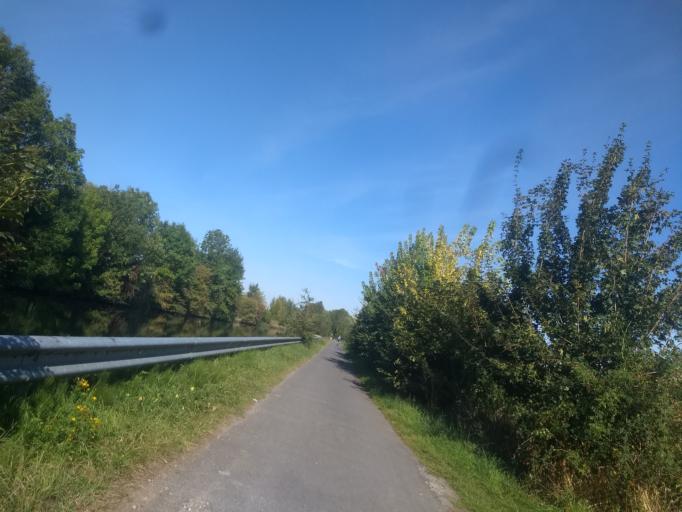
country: FR
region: Nord-Pas-de-Calais
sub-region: Departement du Pas-de-Calais
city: Fampoux
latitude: 50.2976
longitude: 2.8646
